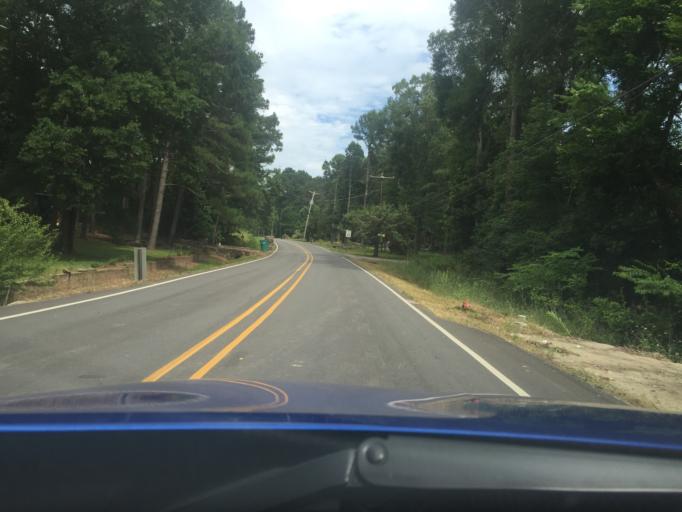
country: US
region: Arkansas
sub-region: Pulaski County
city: Maumelle
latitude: 34.8314
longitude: -92.4481
